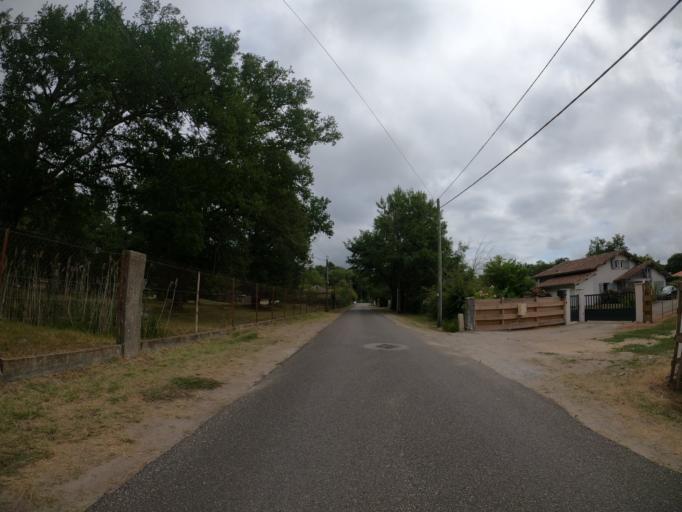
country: FR
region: Aquitaine
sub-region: Departement des Landes
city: Leon
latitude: 43.8844
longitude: -1.3017
